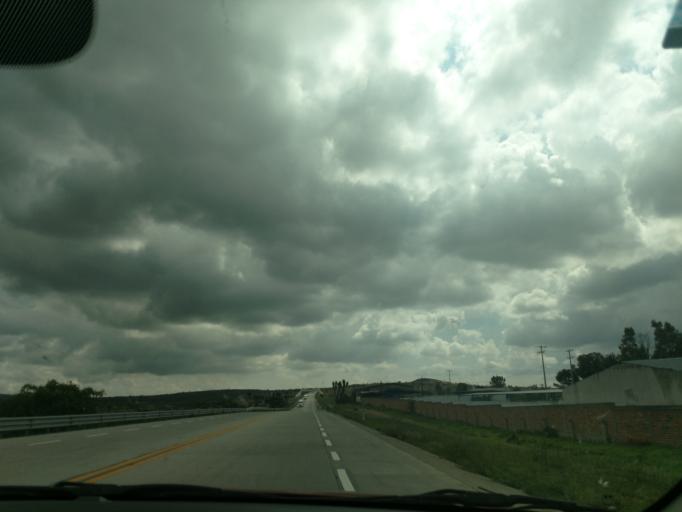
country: MX
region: Jalisco
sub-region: Ojuelos de Jalisco
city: Matanzas
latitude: 21.5645
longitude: -101.6820
